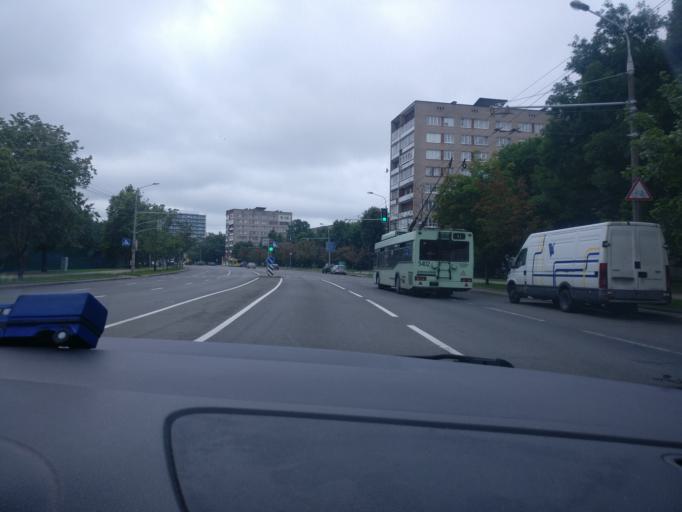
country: BY
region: Minsk
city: Minsk
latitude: 53.8823
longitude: 27.6136
